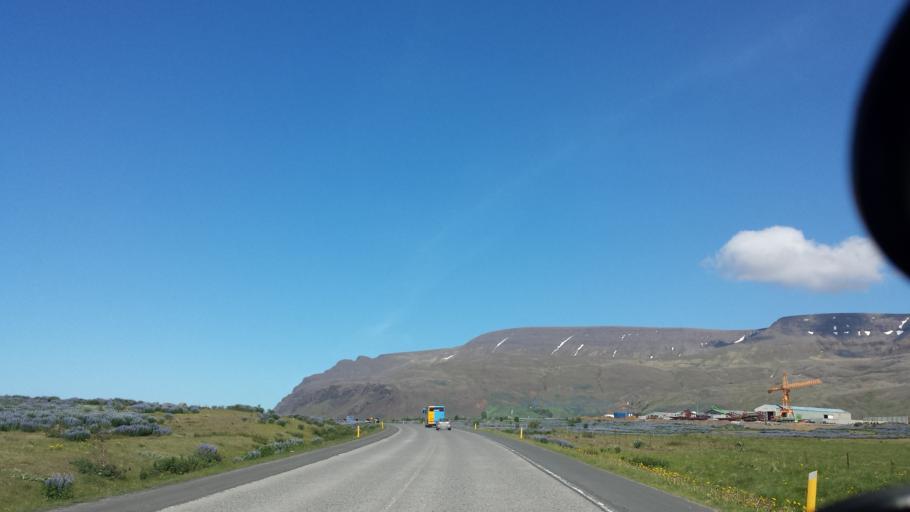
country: IS
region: Capital Region
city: Mosfellsbaer
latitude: 64.1902
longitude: -21.6880
